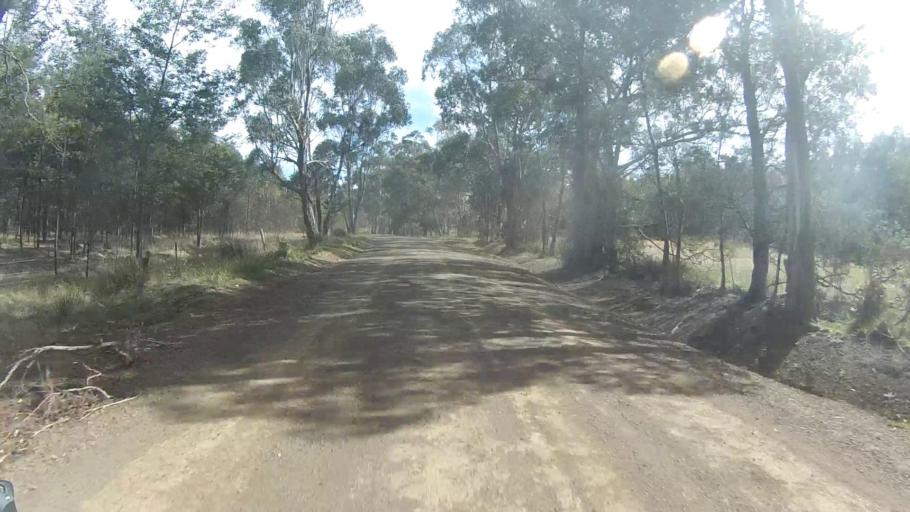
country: AU
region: Tasmania
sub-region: Sorell
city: Sorell
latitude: -42.6576
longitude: 147.8979
